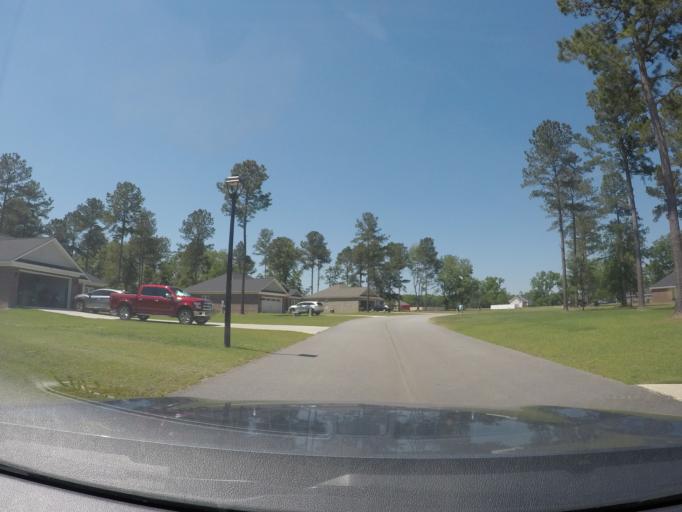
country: US
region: Georgia
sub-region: Bulloch County
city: Statesboro
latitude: 32.3564
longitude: -81.7652
